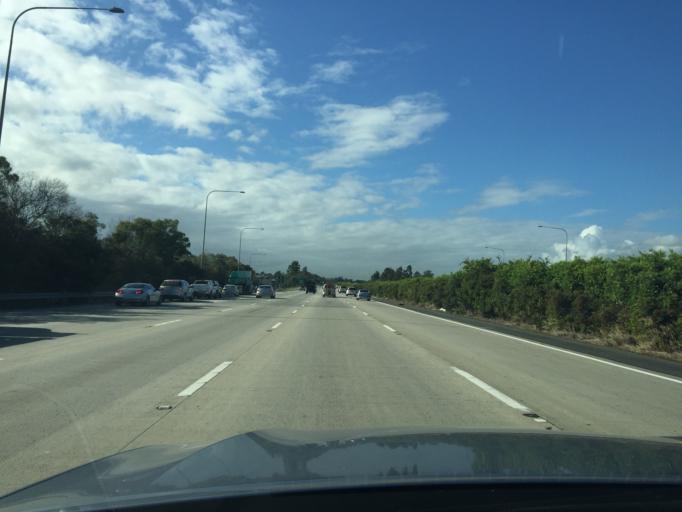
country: AU
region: Queensland
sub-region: Gold Coast
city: Yatala
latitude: -27.7317
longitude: 153.2255
